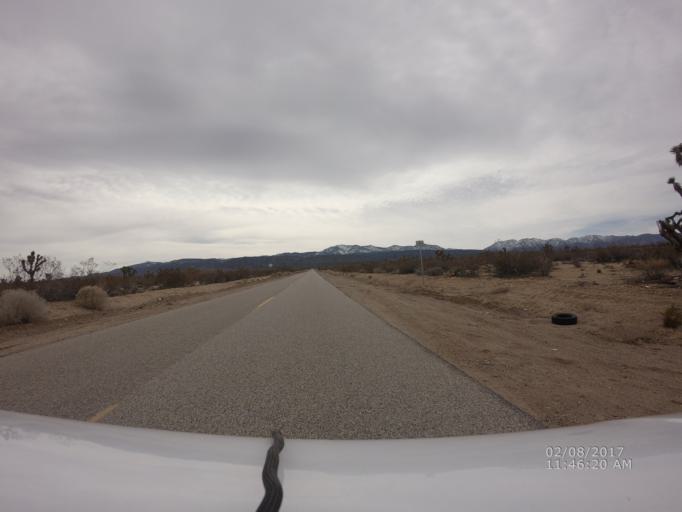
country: US
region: California
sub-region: San Bernardino County
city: Pinon Hills
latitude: 34.4970
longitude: -117.7483
